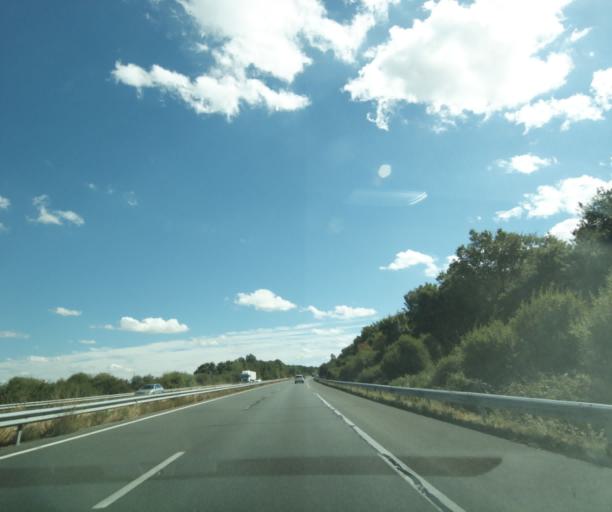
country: FR
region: Aquitaine
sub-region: Departement du Lot-et-Garonne
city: Fourques-sur-Garonne
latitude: 44.4210
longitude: 0.1703
